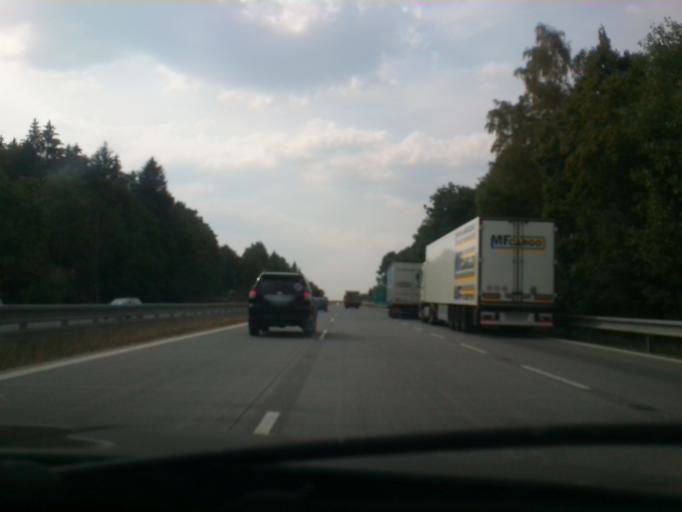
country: CZ
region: Central Bohemia
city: Divisov
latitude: 49.7984
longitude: 14.9163
